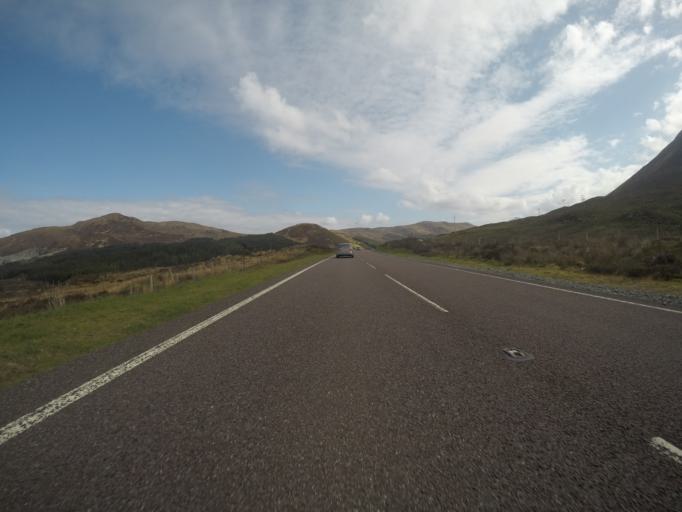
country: GB
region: Scotland
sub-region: Highland
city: Portree
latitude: 57.3085
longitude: -6.0935
